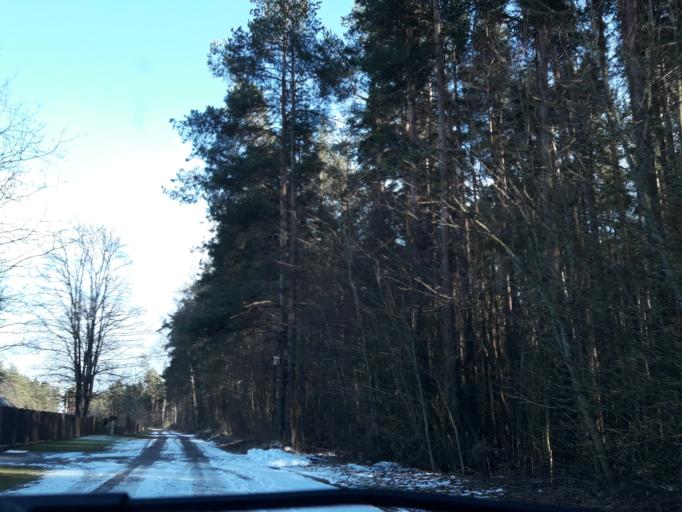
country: LV
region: Kekava
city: Kekava
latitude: 56.8453
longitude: 24.1927
